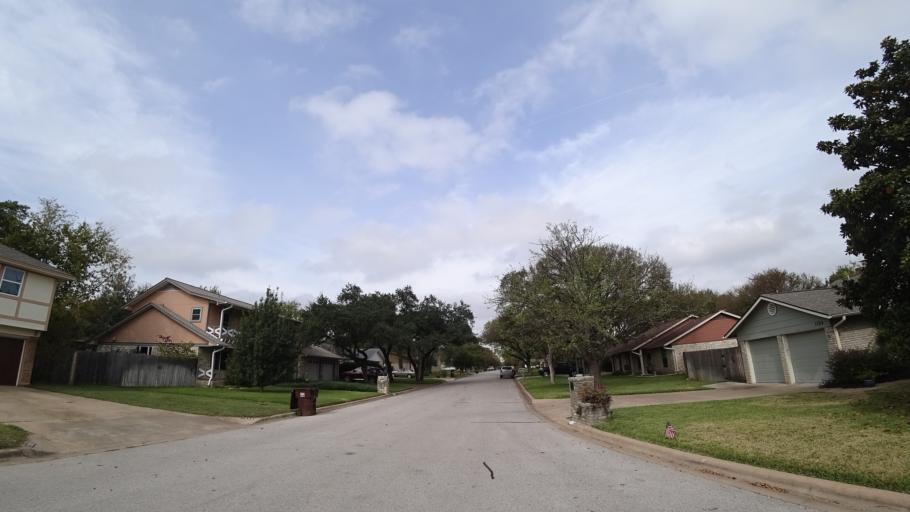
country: US
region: Texas
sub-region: Williamson County
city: Round Rock
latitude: 30.4977
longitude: -97.6889
